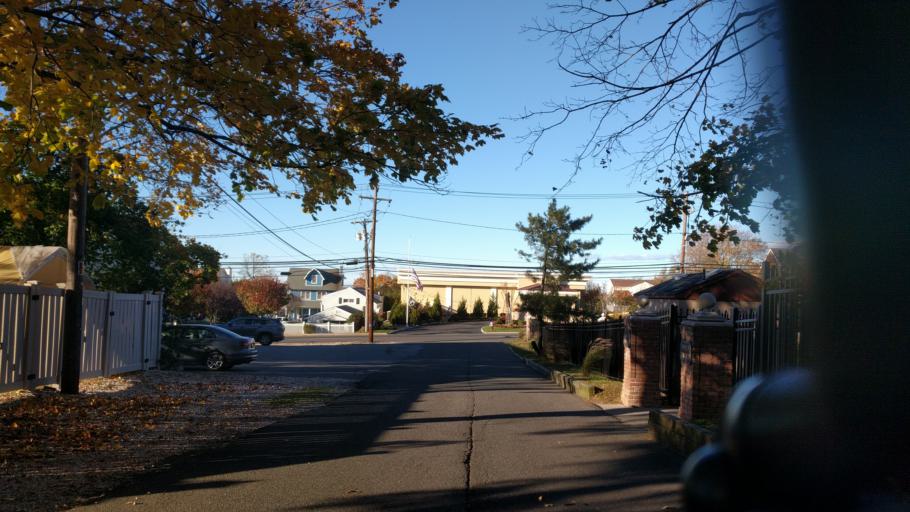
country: US
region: New York
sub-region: Nassau County
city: Bayville
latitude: 40.9092
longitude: -73.5771
